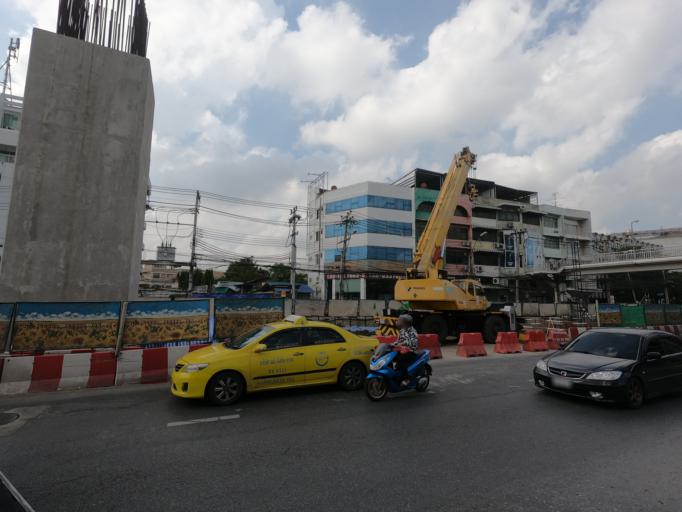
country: TH
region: Bangkok
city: Wang Thonglang
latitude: 13.7783
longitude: 100.6045
